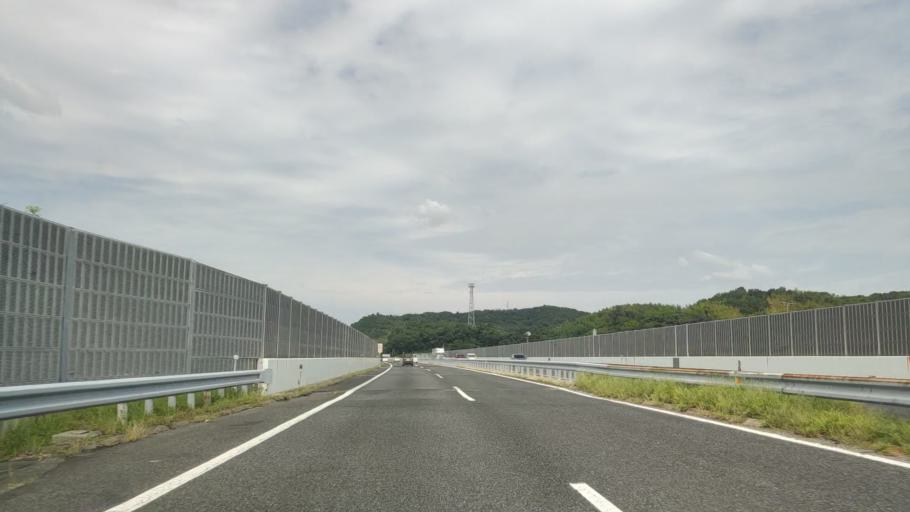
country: JP
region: Wakayama
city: Kainan
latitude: 34.1712
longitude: 135.2351
